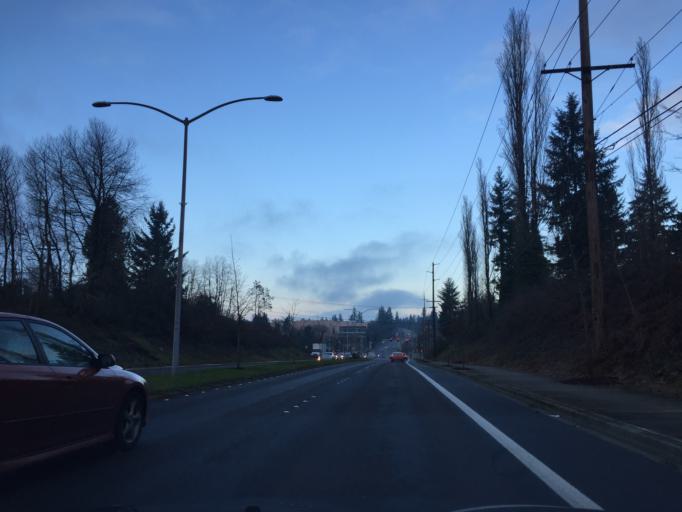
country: US
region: Washington
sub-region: Thurston County
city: Tumwater
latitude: 47.0100
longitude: -122.9056
